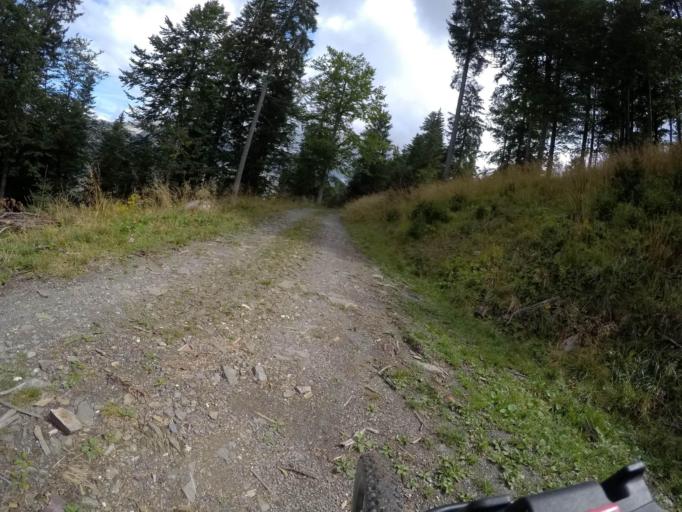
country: IT
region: Friuli Venezia Giulia
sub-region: Provincia di Udine
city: Paularo
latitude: 46.5147
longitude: 13.2105
